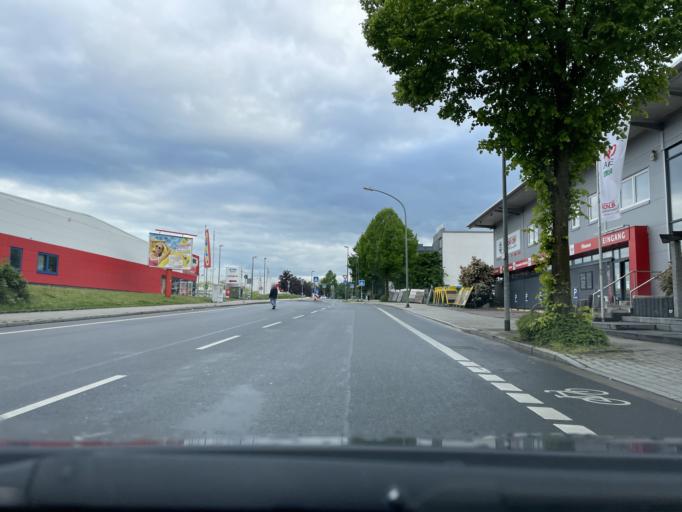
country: DE
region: North Rhine-Westphalia
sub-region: Regierungsbezirk Dusseldorf
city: Essen
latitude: 51.4588
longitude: 6.9830
